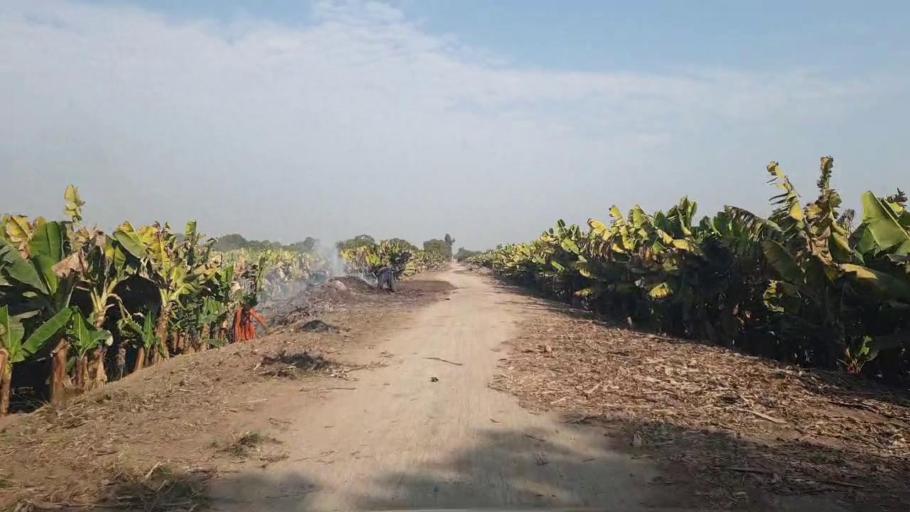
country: PK
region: Sindh
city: Tando Adam
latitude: 25.7564
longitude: 68.5883
